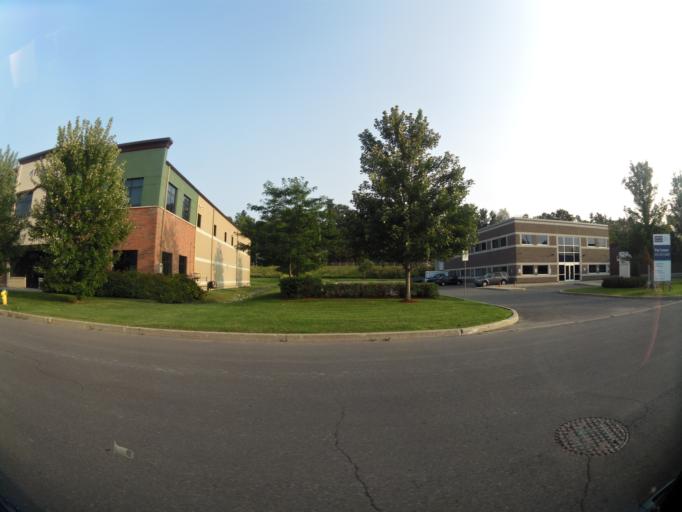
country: CA
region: Ontario
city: Clarence-Rockland
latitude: 45.4893
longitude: -75.4847
